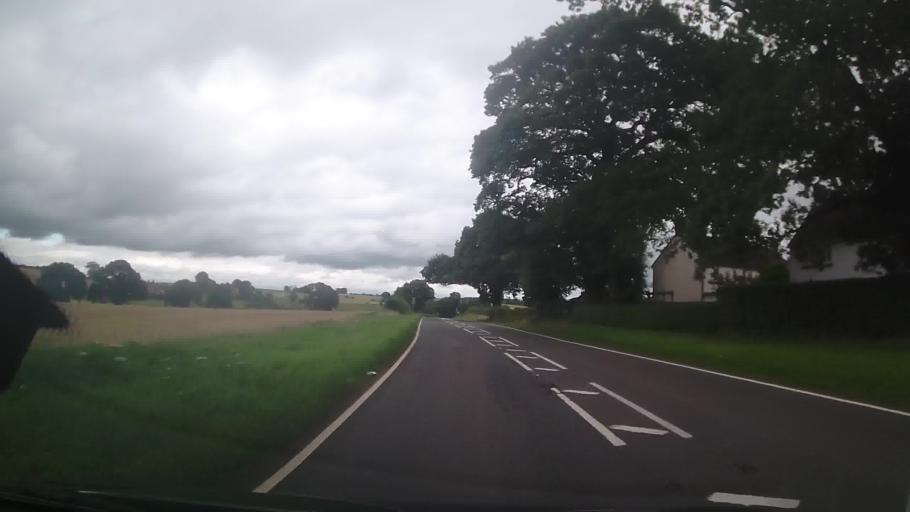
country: GB
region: England
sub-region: Shropshire
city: Ellesmere
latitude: 52.9123
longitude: -2.8363
